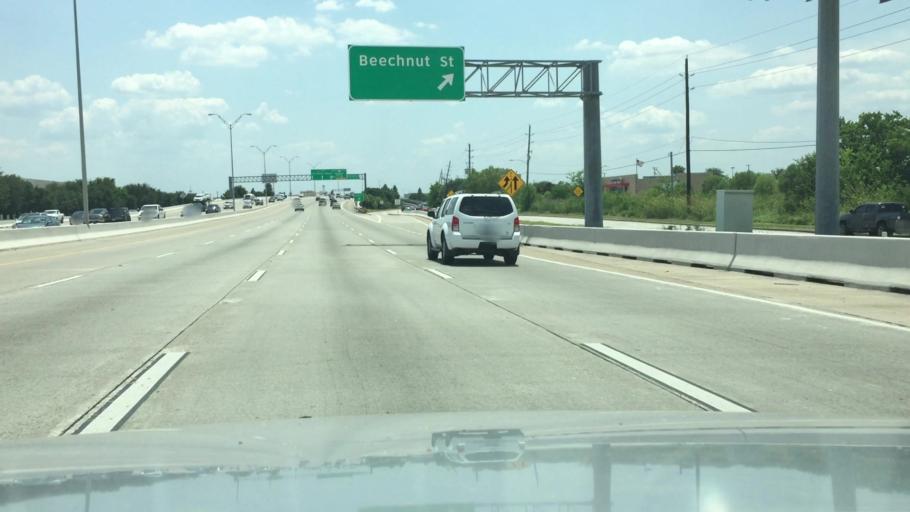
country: US
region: Texas
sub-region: Fort Bend County
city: Meadows Place
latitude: 29.6946
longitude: -95.5572
